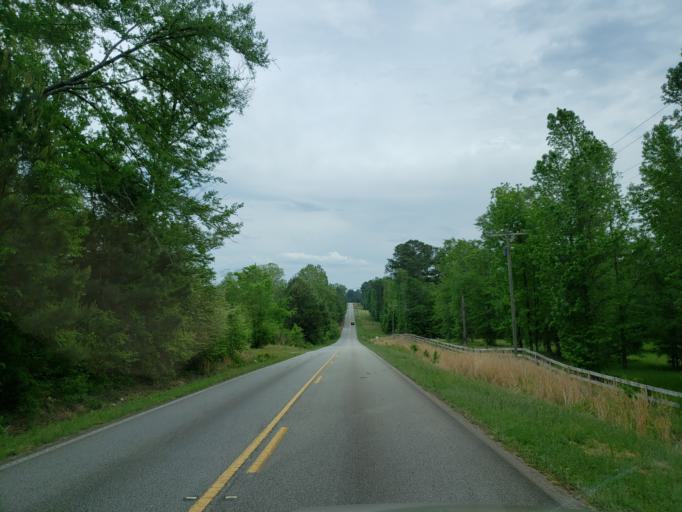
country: US
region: Georgia
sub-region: Bibb County
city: West Point
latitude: 32.8246
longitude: -83.8756
